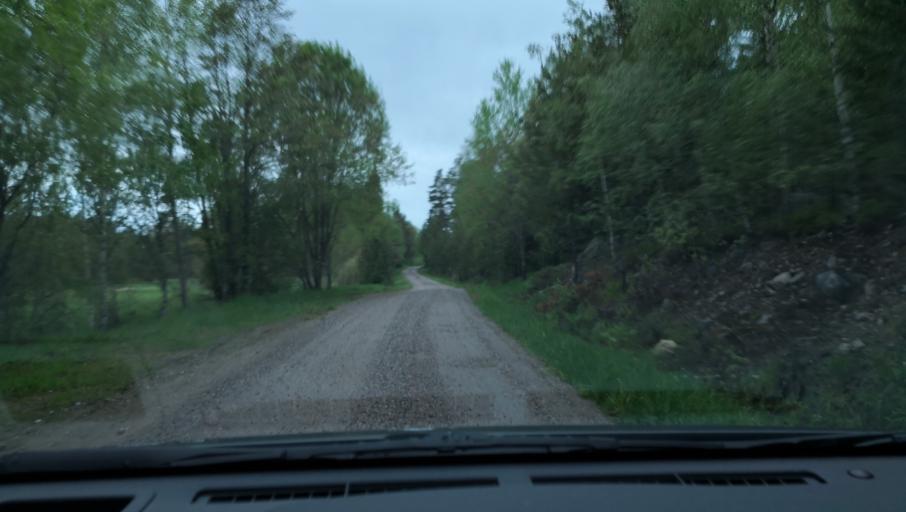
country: SE
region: Uppsala
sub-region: Heby Kommun
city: OEstervala
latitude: 59.9942
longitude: 17.2488
